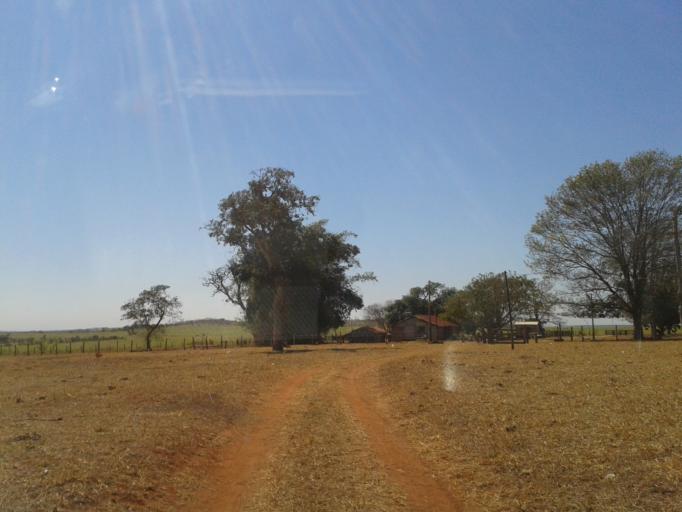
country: BR
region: Minas Gerais
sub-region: Santa Vitoria
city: Santa Vitoria
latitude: -19.1252
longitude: -50.0142
